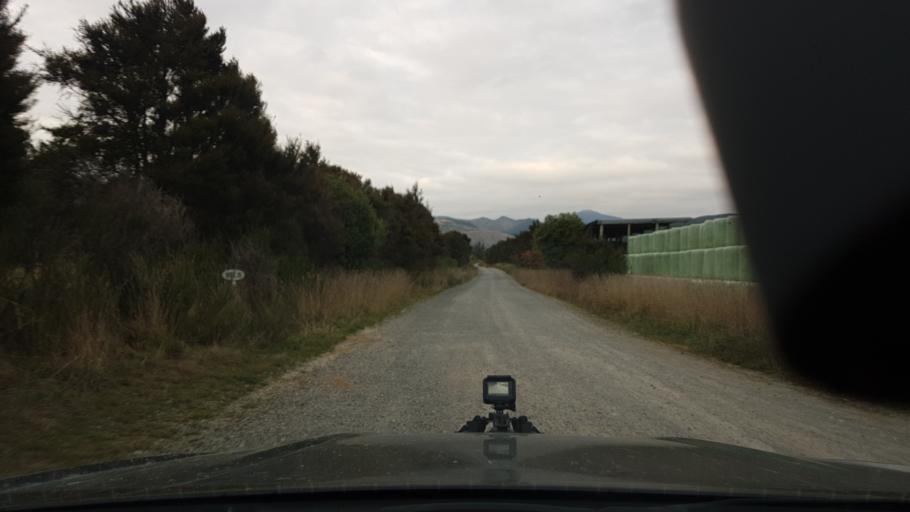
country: NZ
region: Tasman
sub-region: Tasman District
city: Brightwater
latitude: -41.6683
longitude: 173.1936
